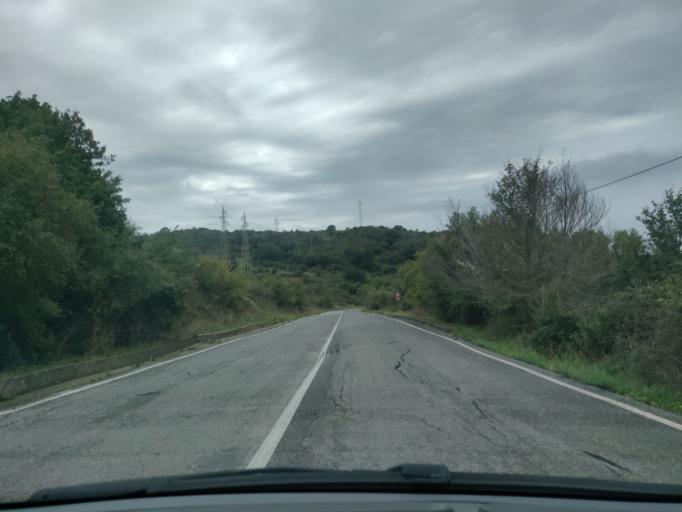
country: IT
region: Latium
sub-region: Citta metropolitana di Roma Capitale
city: Civitavecchia
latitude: 42.1135
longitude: 11.8536
